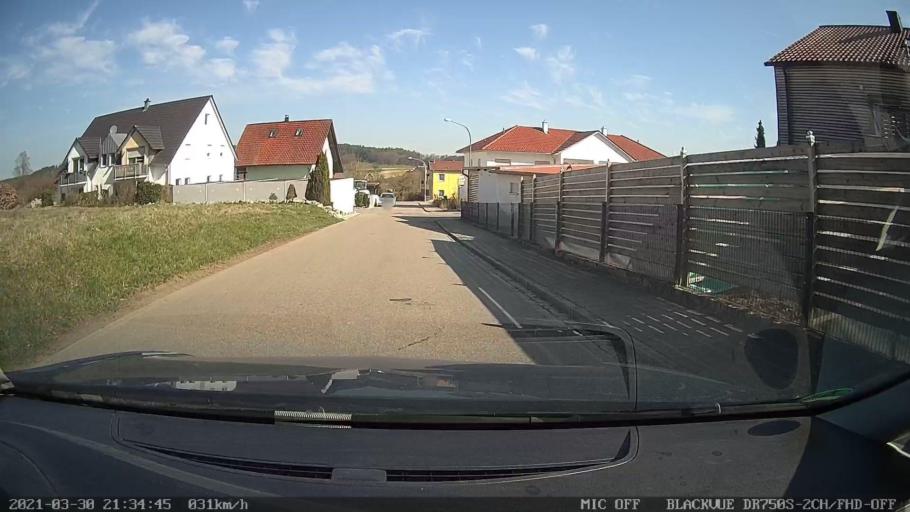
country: DE
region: Bavaria
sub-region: Upper Palatinate
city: Zeitlarn
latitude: 49.0986
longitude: 12.1000
